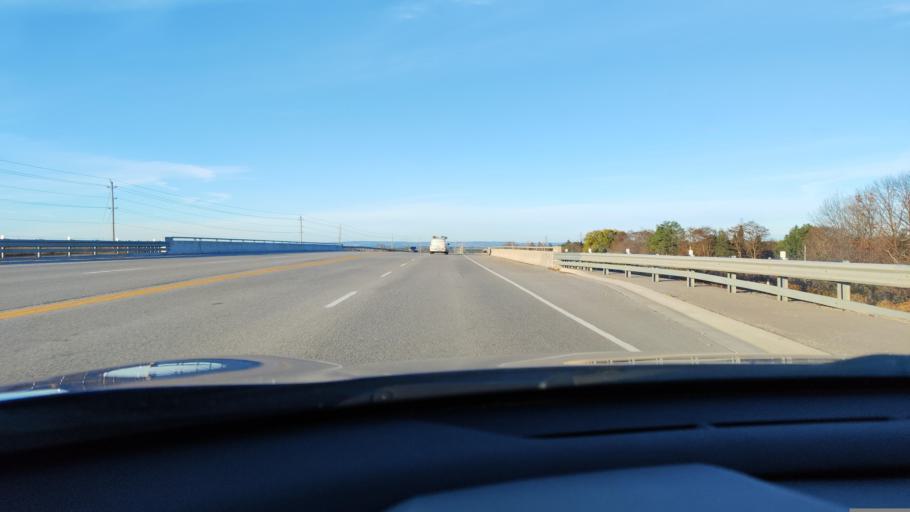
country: CA
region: Ontario
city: Angus
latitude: 44.3438
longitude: -79.8235
